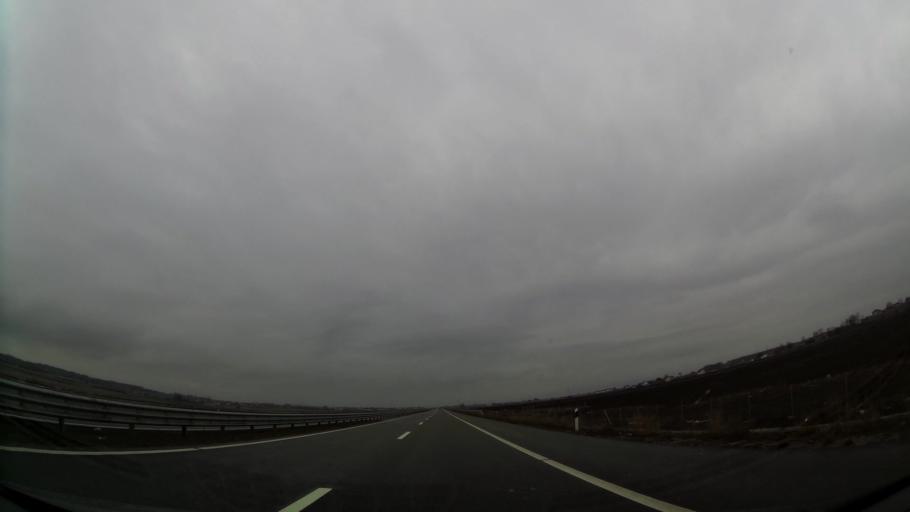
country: XK
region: Ferizaj
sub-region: Komuna e Ferizajt
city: Ferizaj
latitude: 42.4230
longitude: 21.1989
